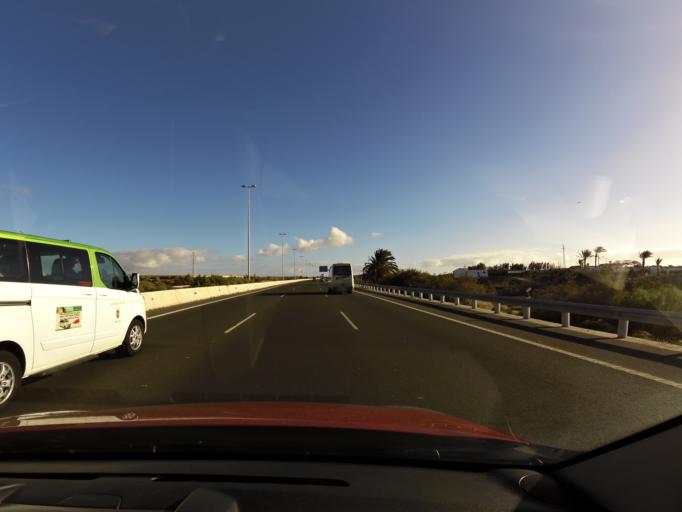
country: ES
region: Canary Islands
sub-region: Provincia de Las Palmas
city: Cruce de Arinaga
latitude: 27.8148
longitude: -15.4728
